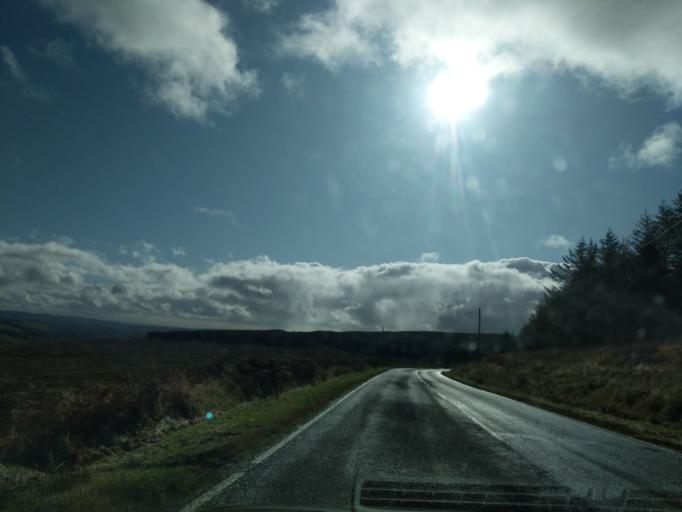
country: GB
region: Scotland
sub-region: Dumfries and Galloway
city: Moffat
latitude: 55.3910
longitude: -3.4839
